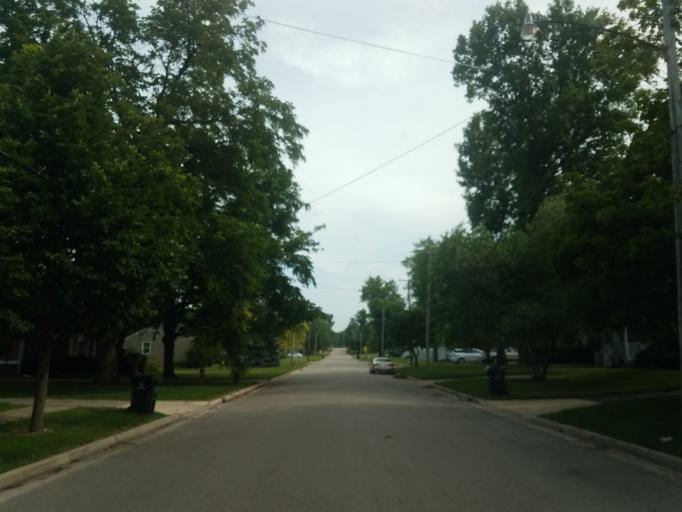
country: US
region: Illinois
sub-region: McLean County
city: Bloomington
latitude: 40.4720
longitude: -88.9677
